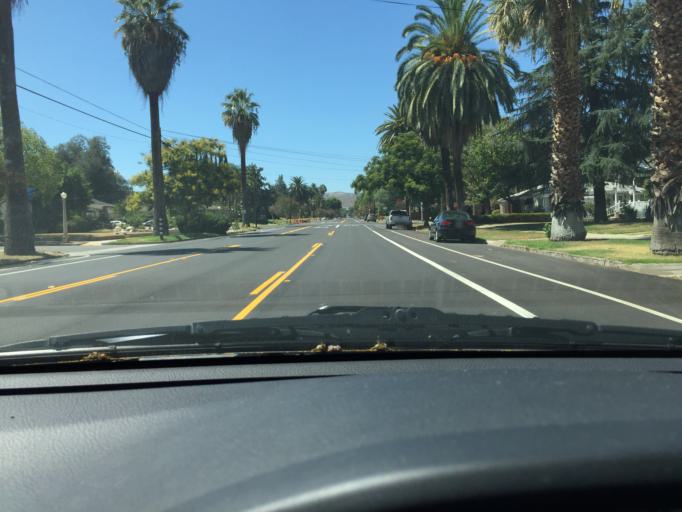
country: US
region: California
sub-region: San Bernardino County
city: Redlands
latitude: 34.0489
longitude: -117.1817
